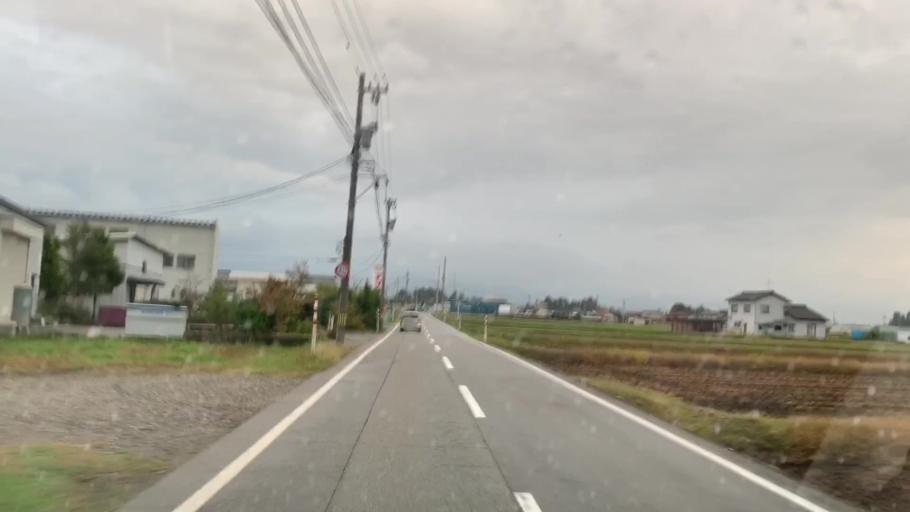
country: JP
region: Toyama
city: Kamiichi
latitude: 36.6500
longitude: 137.3285
